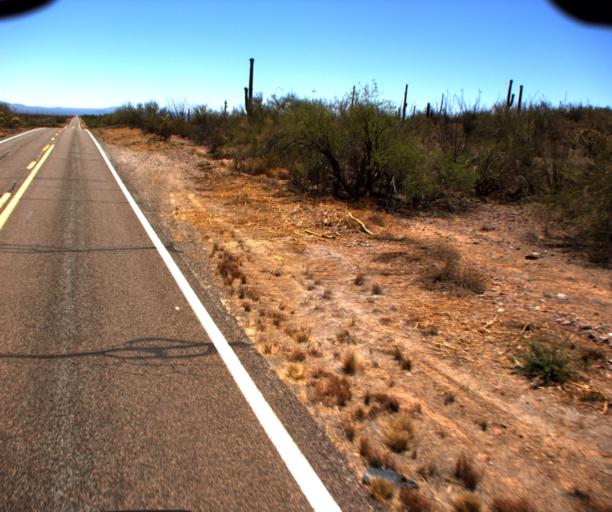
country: US
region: Arizona
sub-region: Pima County
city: Ajo
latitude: 32.2044
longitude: -112.5297
